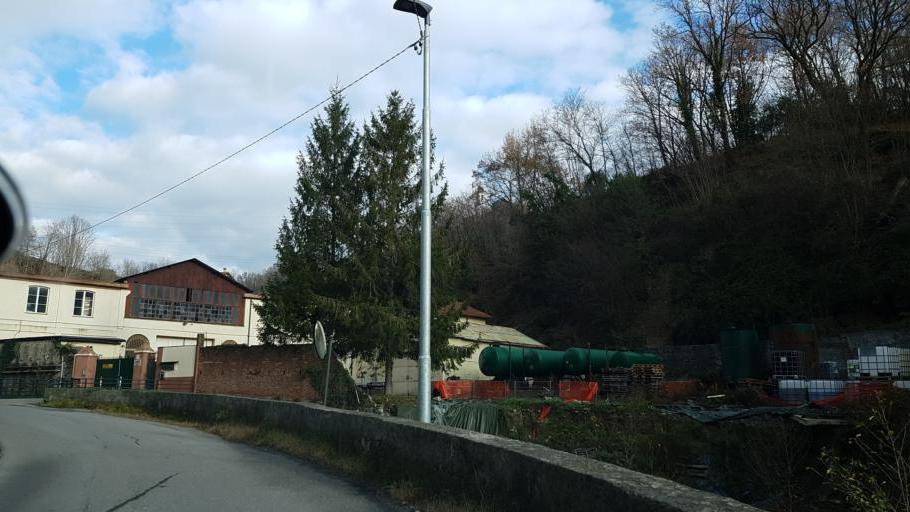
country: IT
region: Liguria
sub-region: Provincia di Genova
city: Santa Marta
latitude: 44.4789
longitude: 8.8879
